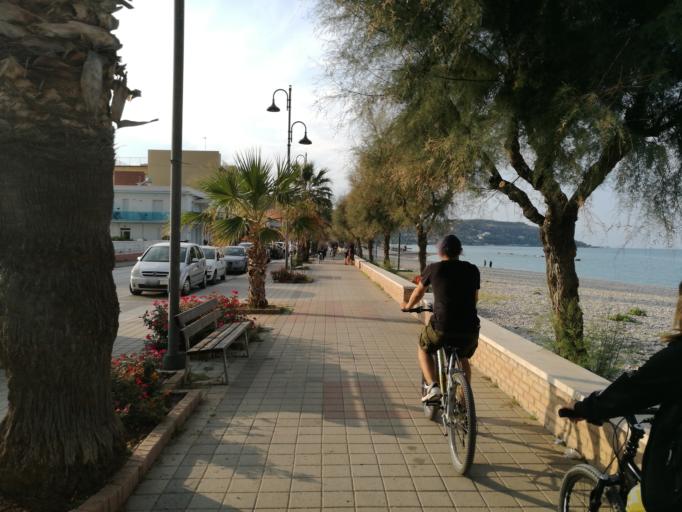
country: IT
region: Abruzzo
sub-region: Provincia di Chieti
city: Fossacesia
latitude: 42.2495
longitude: 14.5120
